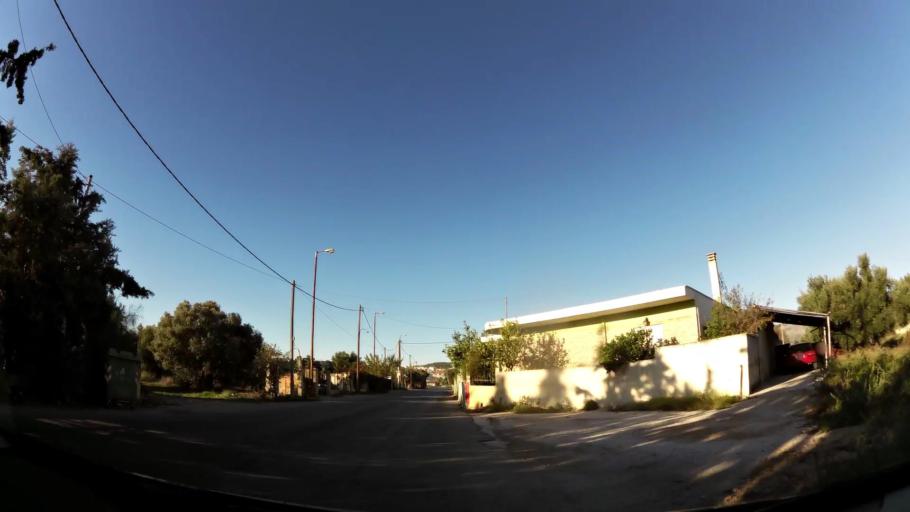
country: GR
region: Attica
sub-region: Nomarchia Anatolikis Attikis
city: Koropi
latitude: 37.9080
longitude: 23.8865
